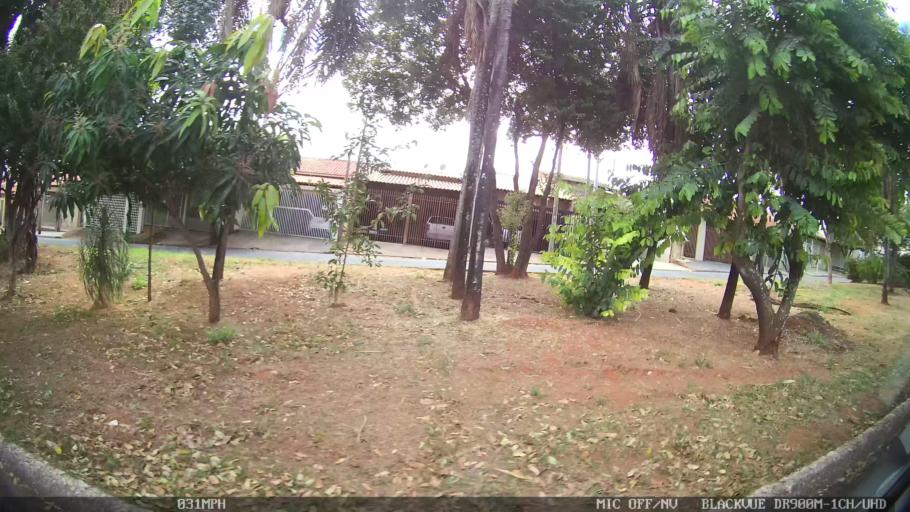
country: BR
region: Sao Paulo
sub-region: Sao Jose Do Rio Preto
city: Sao Jose do Rio Preto
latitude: -20.8075
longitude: -49.4992
